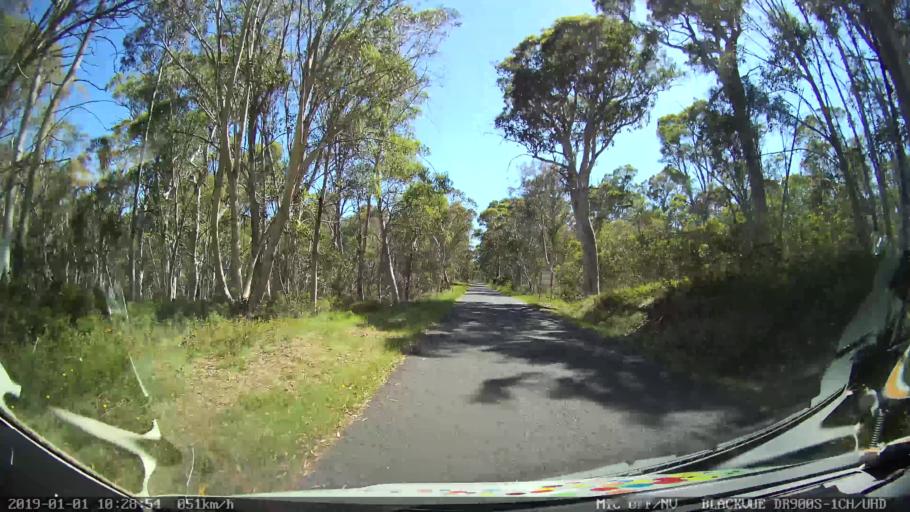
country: AU
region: New South Wales
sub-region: Snowy River
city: Jindabyne
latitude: -36.0578
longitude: 148.2439
